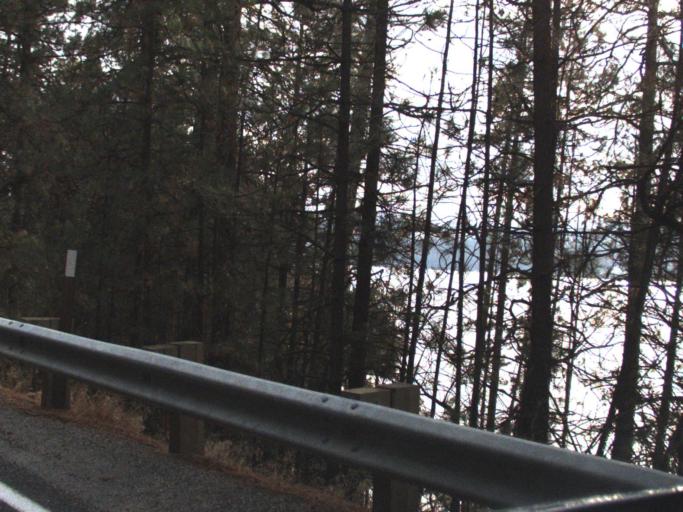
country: US
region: Washington
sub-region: Stevens County
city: Kettle Falls
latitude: 48.3099
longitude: -118.1484
